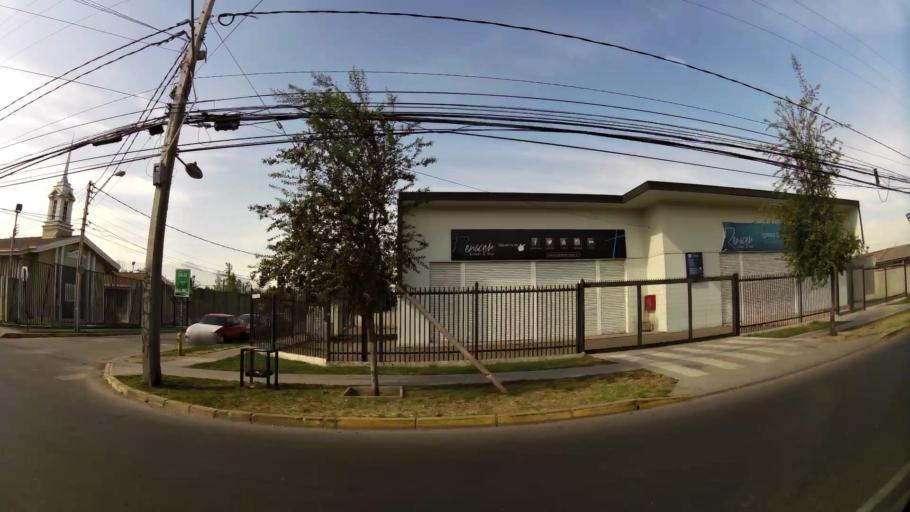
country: CL
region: Santiago Metropolitan
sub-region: Provincia de Cordillera
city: Puente Alto
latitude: -33.5624
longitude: -70.5768
